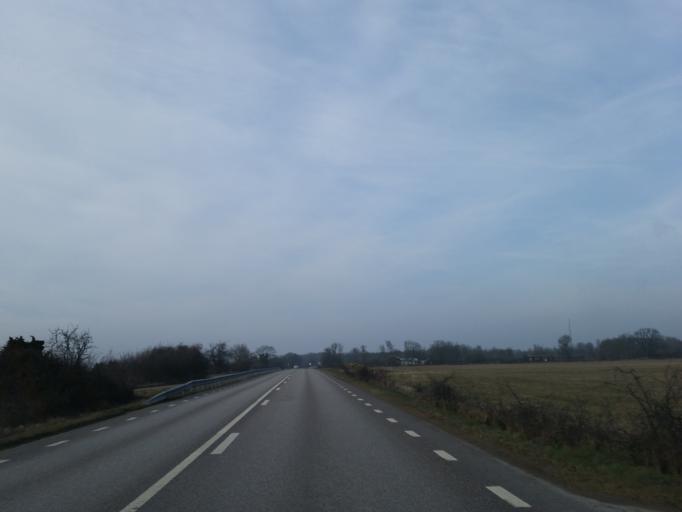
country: SE
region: Kalmar
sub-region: Borgholms Kommun
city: Borgholm
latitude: 56.8910
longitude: 16.7324
